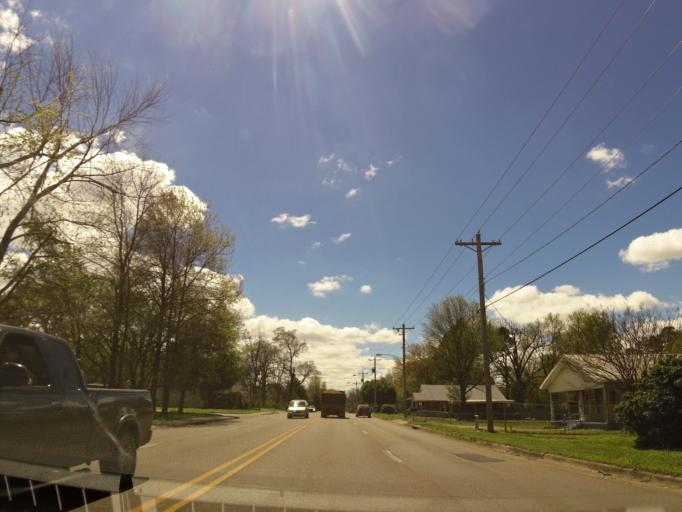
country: US
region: Arkansas
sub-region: Craighead County
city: Jonesboro
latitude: 35.8561
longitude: -90.7034
